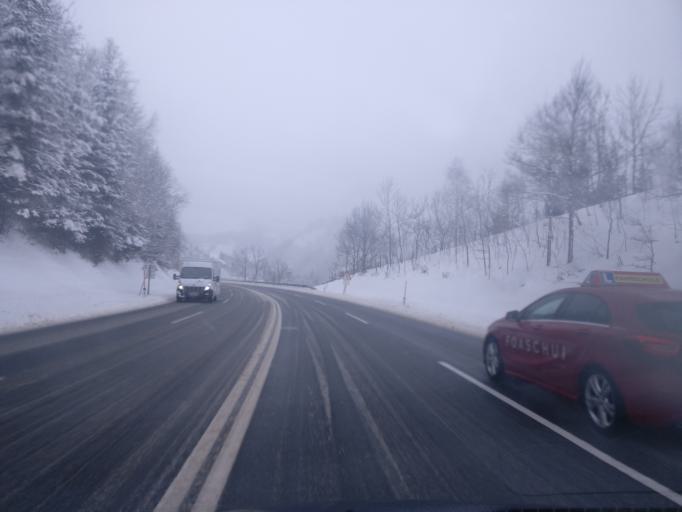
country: AT
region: Salzburg
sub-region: Politischer Bezirk Zell am See
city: Lend
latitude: 47.2984
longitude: 13.0409
